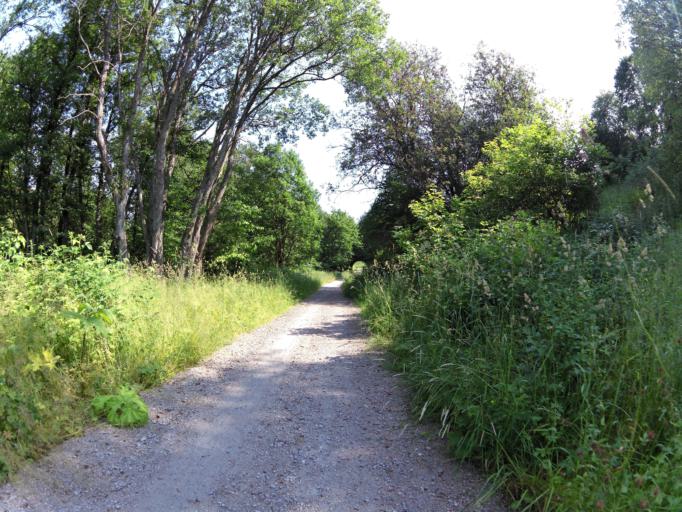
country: NO
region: Ostfold
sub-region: Sarpsborg
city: Sarpsborg
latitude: 59.2623
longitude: 11.1122
